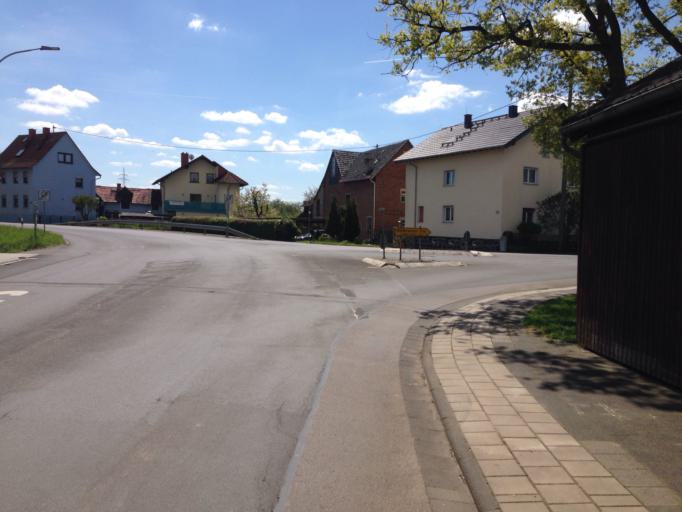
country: DE
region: Hesse
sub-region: Regierungsbezirk Giessen
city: Hungen
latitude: 50.4910
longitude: 8.8545
